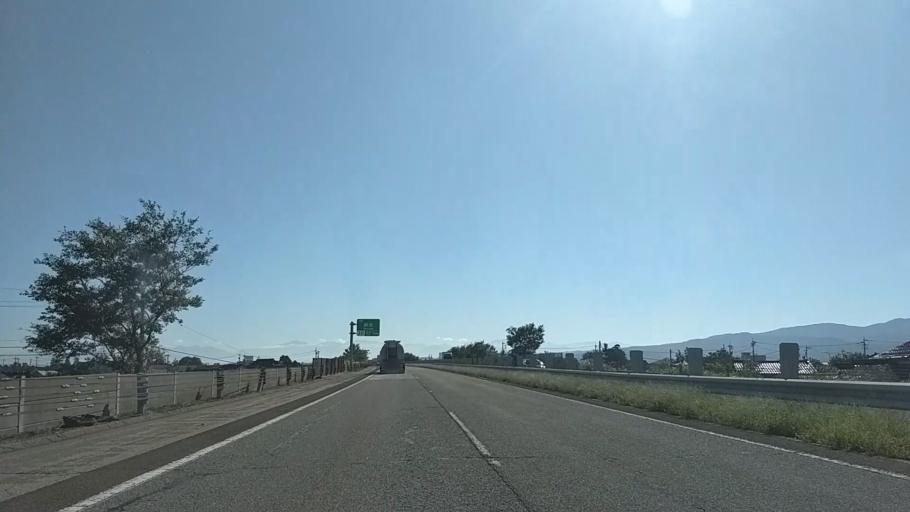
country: JP
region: Toyama
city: Nanto-shi
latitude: 36.6233
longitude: 136.9384
